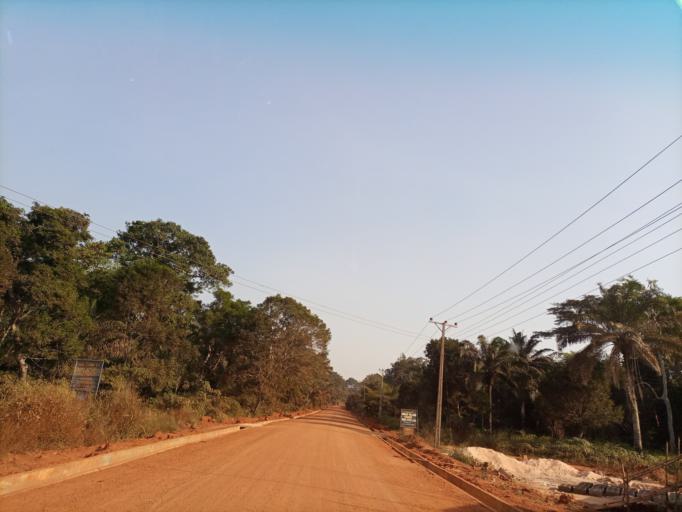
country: NG
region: Enugu
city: Opi
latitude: 6.7556
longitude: 7.4049
